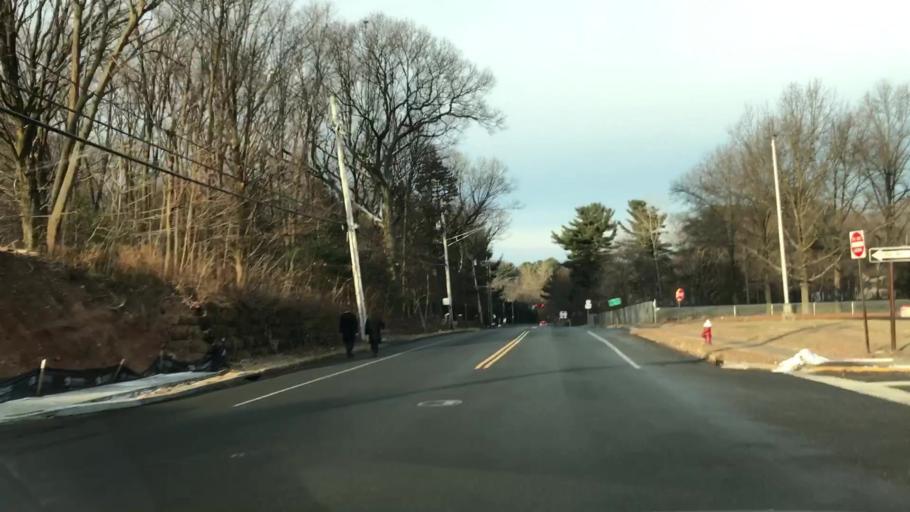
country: US
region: New York
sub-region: Rockland County
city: Kaser
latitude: 41.1351
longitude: -74.0635
